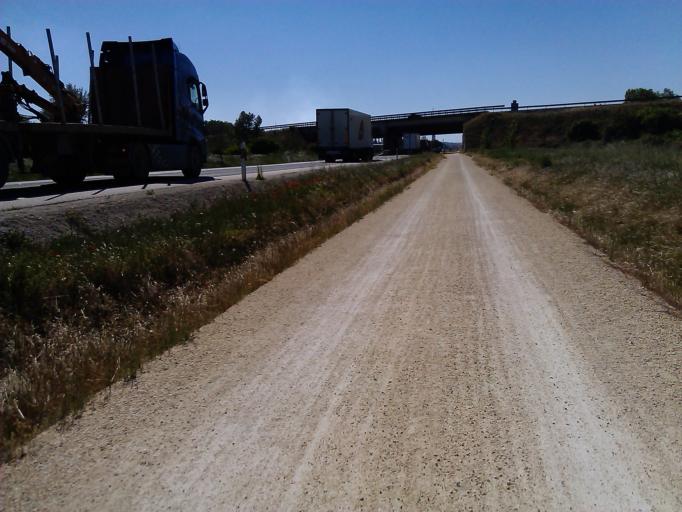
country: ES
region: Castille and Leon
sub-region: Provincia de Burgos
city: Cardenajimeno
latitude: 42.3405
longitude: -3.6066
